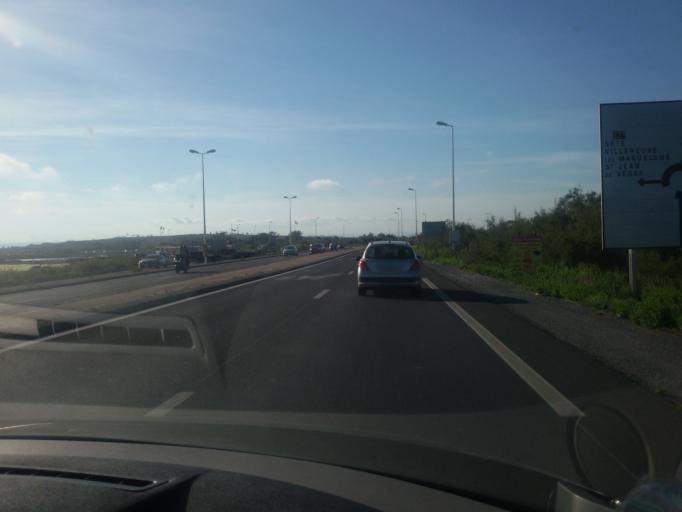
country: FR
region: Languedoc-Roussillon
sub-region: Departement de l'Herault
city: Palavas-les-Flots
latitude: 43.5383
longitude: 3.9003
